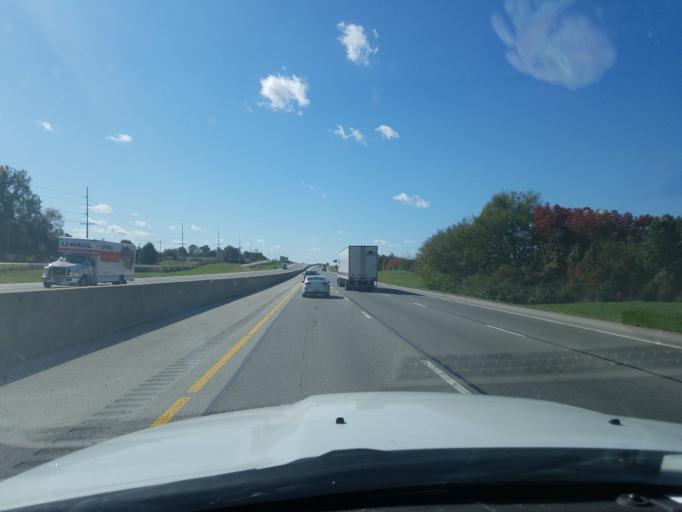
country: US
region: Kentucky
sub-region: Warren County
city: Bowling Green
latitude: 36.9701
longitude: -86.3951
